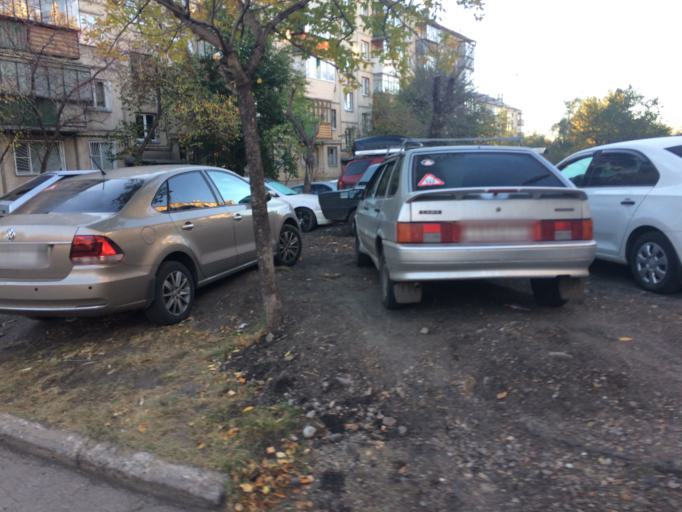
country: RU
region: Chelyabinsk
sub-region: Gorod Magnitogorsk
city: Magnitogorsk
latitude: 53.4042
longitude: 58.9737
